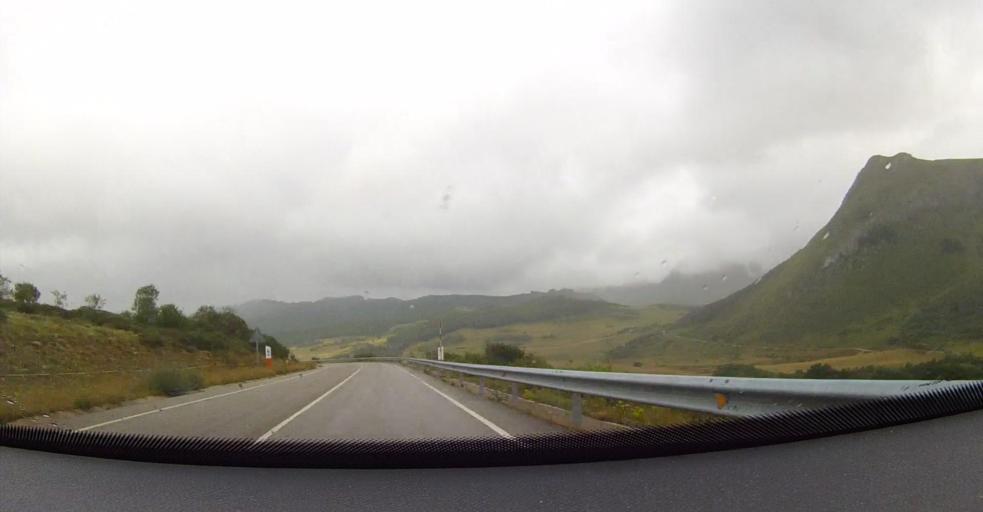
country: ES
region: Castille and Leon
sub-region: Provincia de Leon
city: Marana
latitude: 43.0733
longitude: -5.2102
